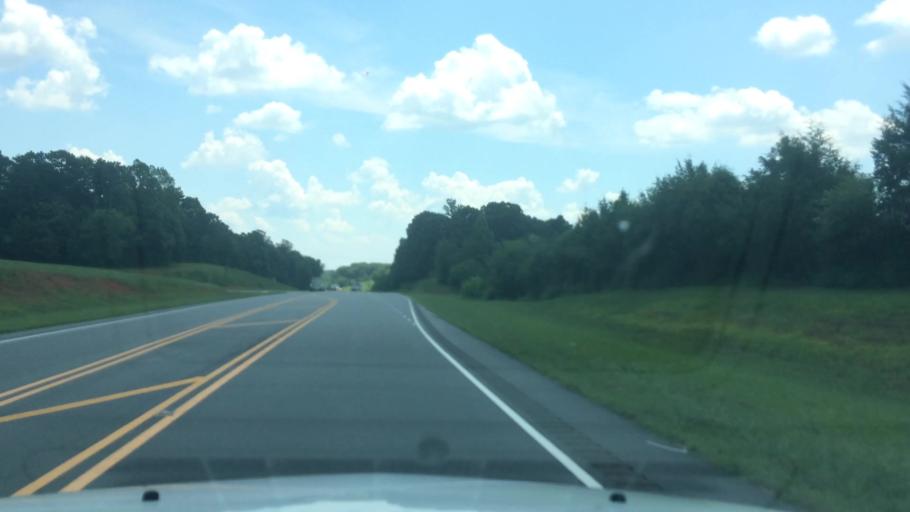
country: US
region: North Carolina
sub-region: Alexander County
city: Stony Point
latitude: 35.8711
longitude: -81.0649
